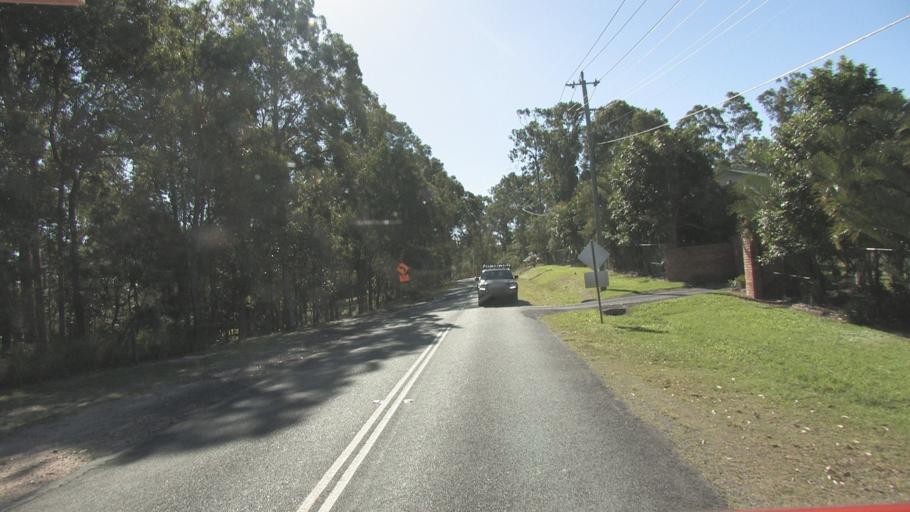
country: AU
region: Queensland
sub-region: Logan
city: Springwood
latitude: -27.6056
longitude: 153.1731
